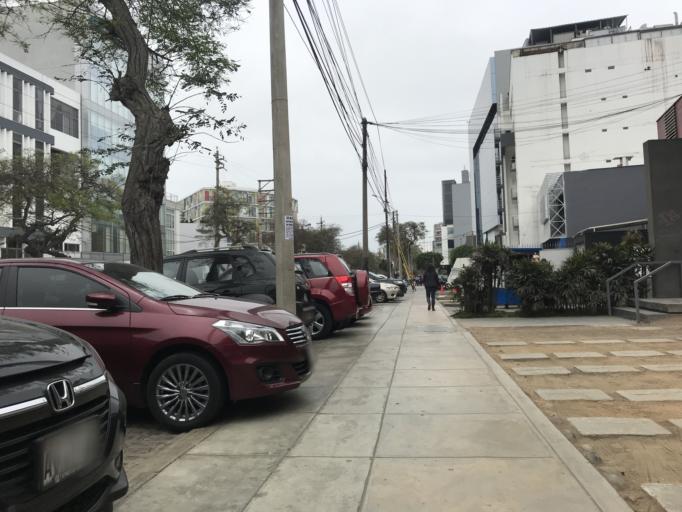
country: PE
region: Lima
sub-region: Lima
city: San Isidro
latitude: -12.1113
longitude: -77.0378
